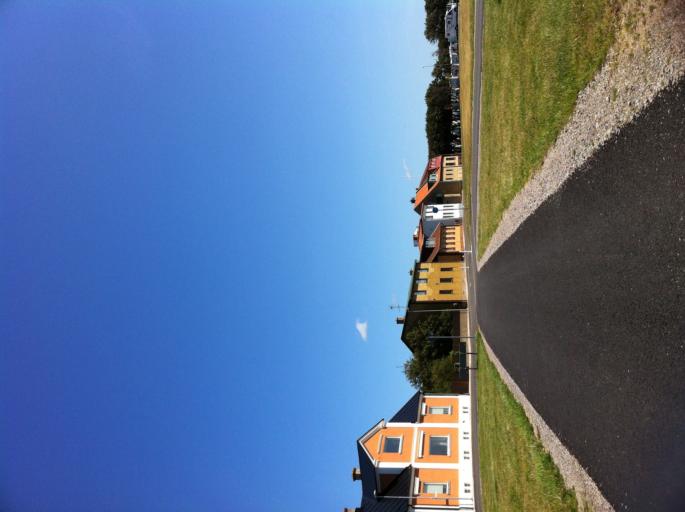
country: SE
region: Skane
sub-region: Hoganas Kommun
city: Hoganas
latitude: 56.2004
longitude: 12.5451
